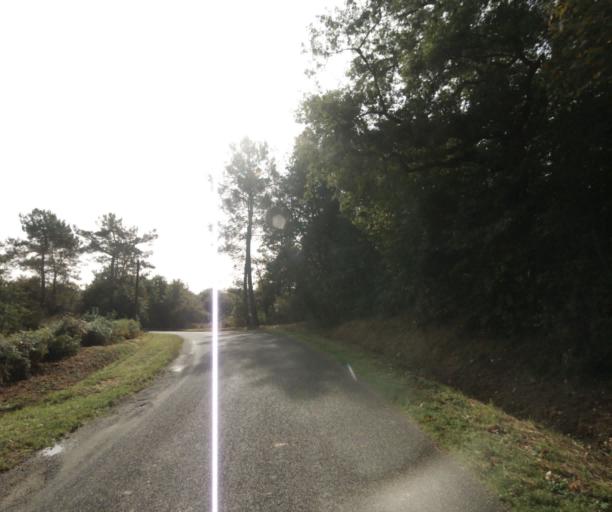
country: FR
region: Midi-Pyrenees
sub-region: Departement du Gers
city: Eauze
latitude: 43.9145
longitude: 0.1356
